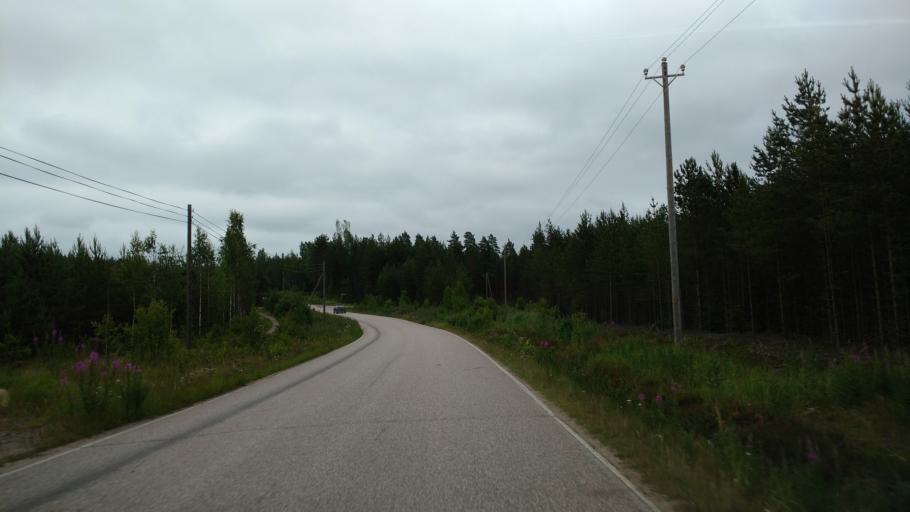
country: FI
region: Varsinais-Suomi
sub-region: Salo
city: Kiikala
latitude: 60.4426
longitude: 23.6229
